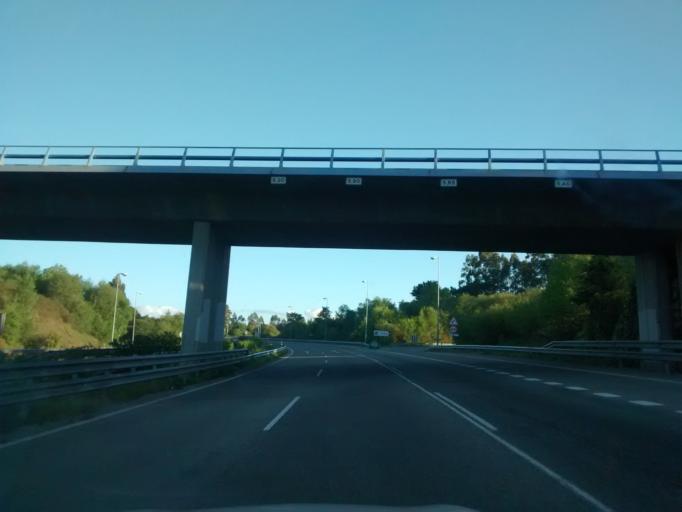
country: ES
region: Asturias
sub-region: Province of Asturias
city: Colunga
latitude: 43.5033
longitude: -5.3306
